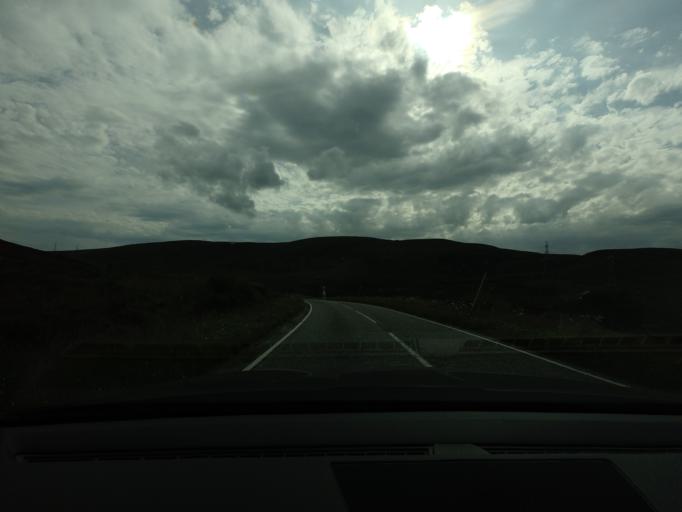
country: GB
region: Scotland
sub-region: Highland
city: Alness
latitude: 57.8359
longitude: -4.2728
